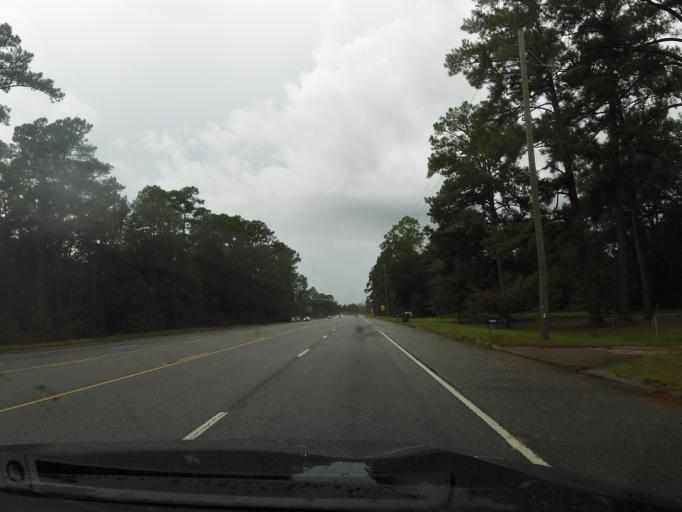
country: US
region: Georgia
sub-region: Wayne County
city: Jesup
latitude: 31.5571
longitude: -81.8248
